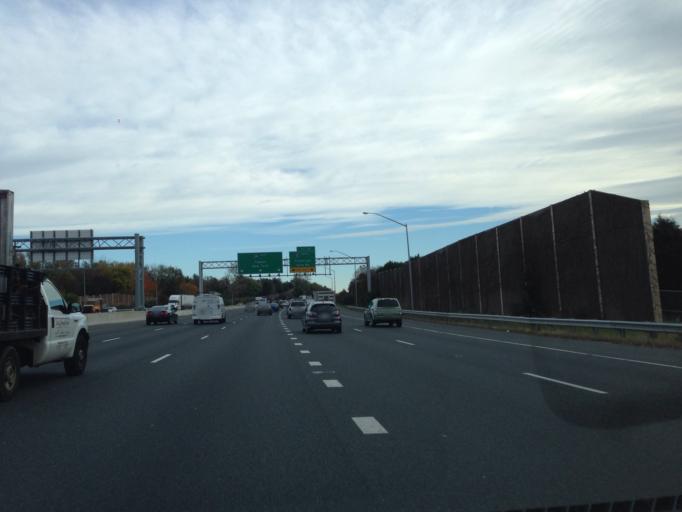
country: US
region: Maryland
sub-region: Baltimore County
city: Mays Chapel
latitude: 39.4150
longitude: -76.6597
